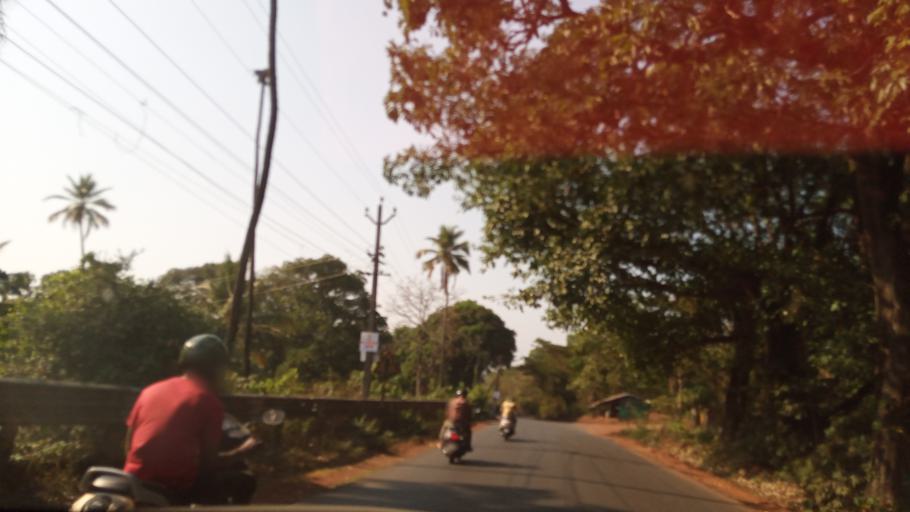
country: IN
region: Goa
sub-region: North Goa
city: Jua
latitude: 15.4779
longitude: 73.9622
